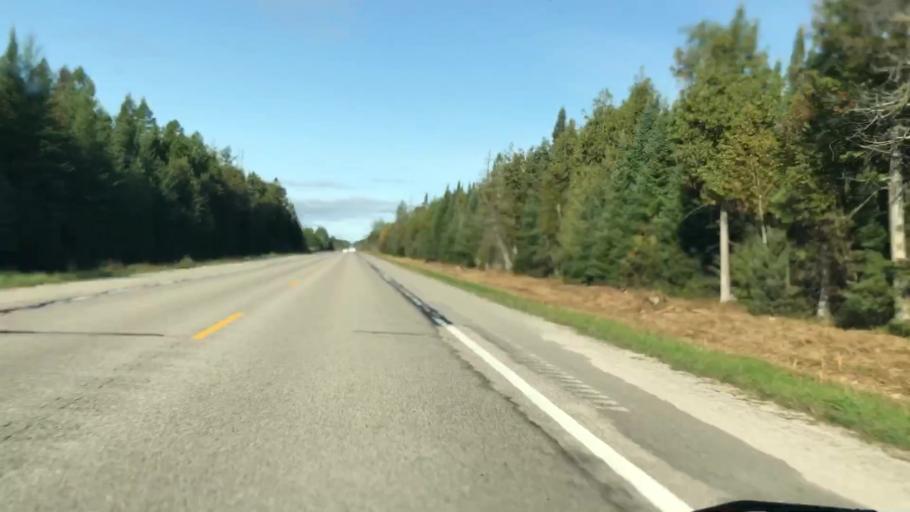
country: US
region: Michigan
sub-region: Luce County
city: Newberry
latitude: 46.3036
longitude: -85.3077
